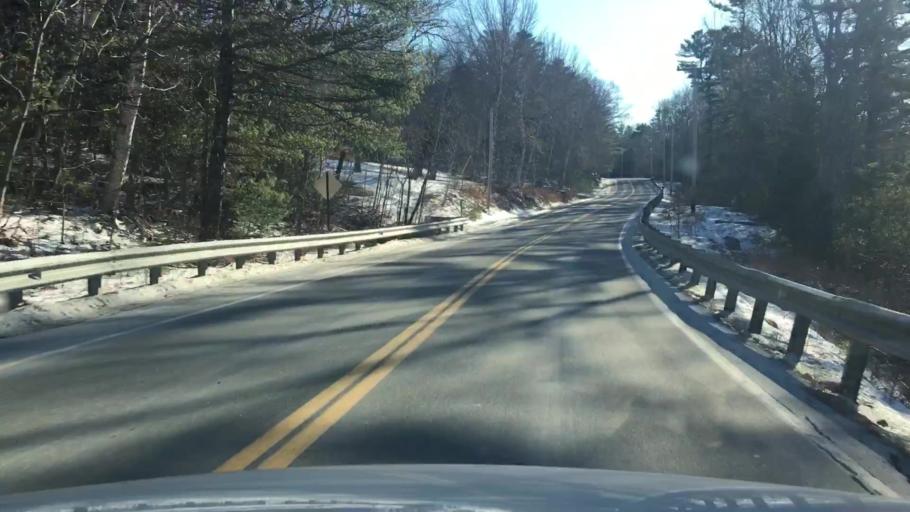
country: US
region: Maine
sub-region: Hancock County
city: Orland
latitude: 44.5411
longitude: -68.7454
